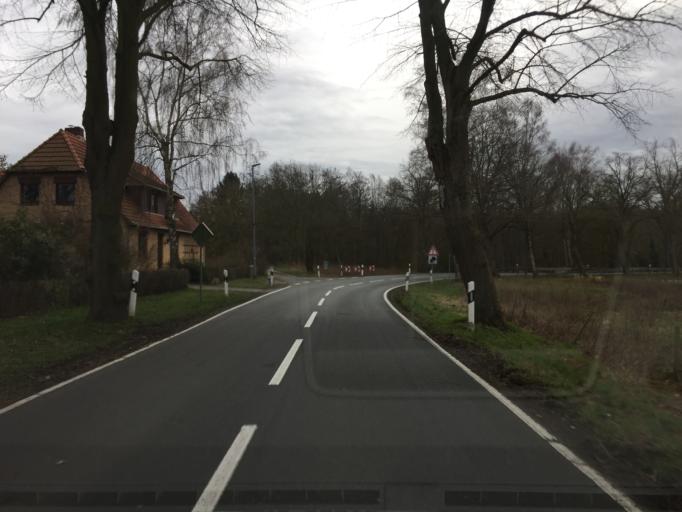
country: DE
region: Lower Saxony
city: Sudwalde
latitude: 52.8337
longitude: 8.8419
